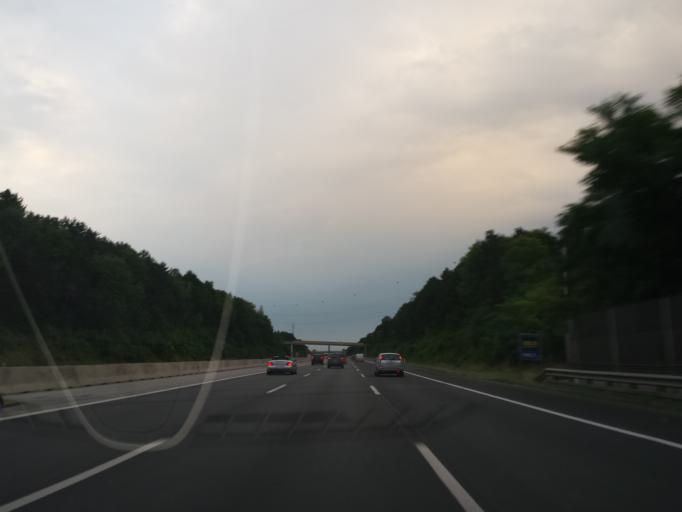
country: AT
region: Lower Austria
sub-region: Politischer Bezirk Wiener Neustadt
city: Theresienfeld
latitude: 47.8693
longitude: 16.1941
